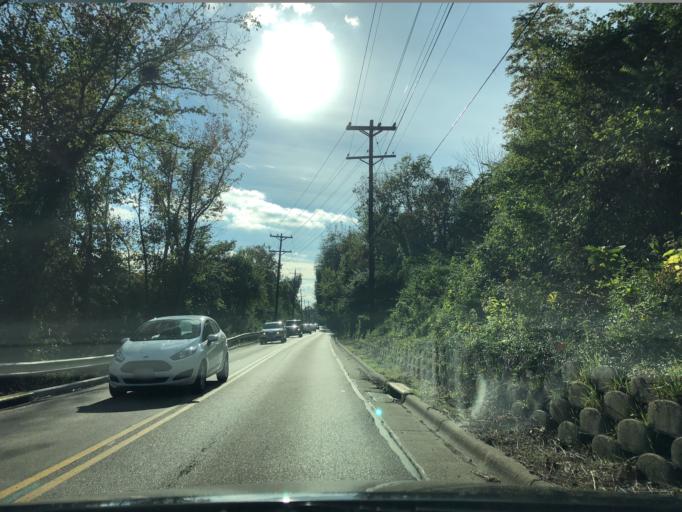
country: US
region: Ohio
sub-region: Hamilton County
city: Loveland
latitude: 39.2563
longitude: -84.2761
